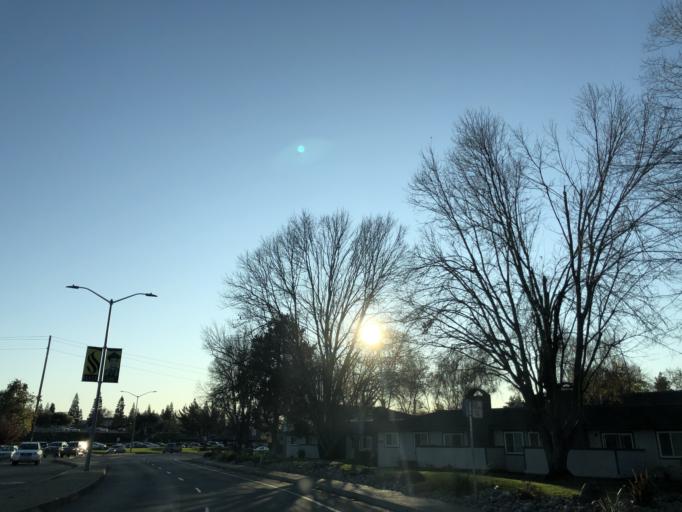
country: US
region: California
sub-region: Sacramento County
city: Rosemont
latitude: 38.5553
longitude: -121.4109
